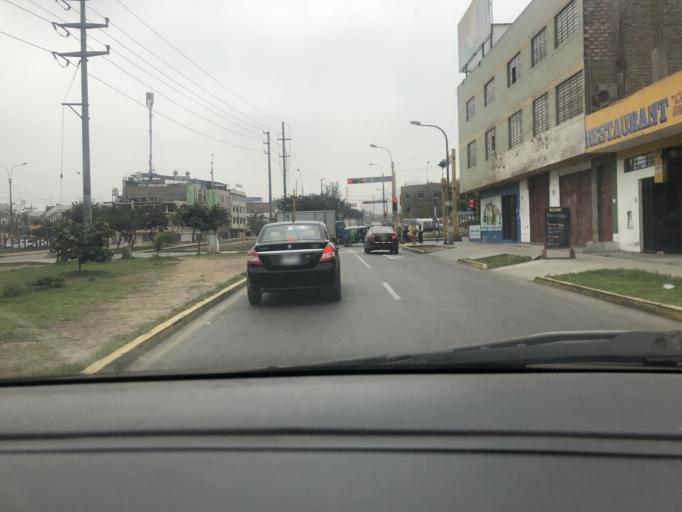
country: PE
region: Lima
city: Lima
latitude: -12.0354
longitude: -76.9983
